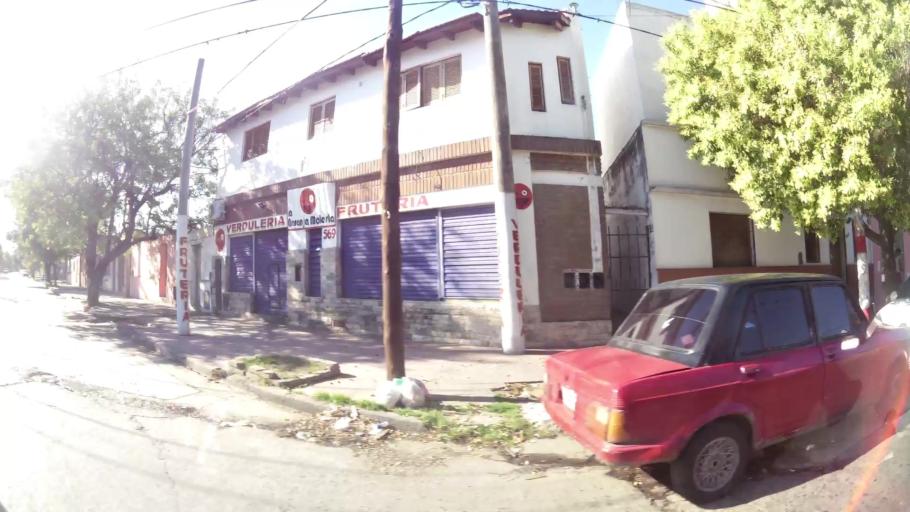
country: AR
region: Cordoba
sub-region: Departamento de Capital
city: Cordoba
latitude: -31.3890
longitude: -64.1722
